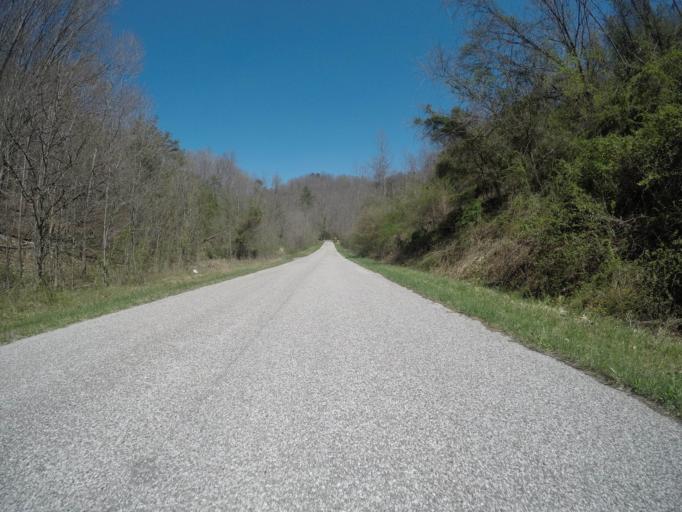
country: US
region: West Virginia
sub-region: Kanawha County
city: Charleston
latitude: 38.4023
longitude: -81.5909
